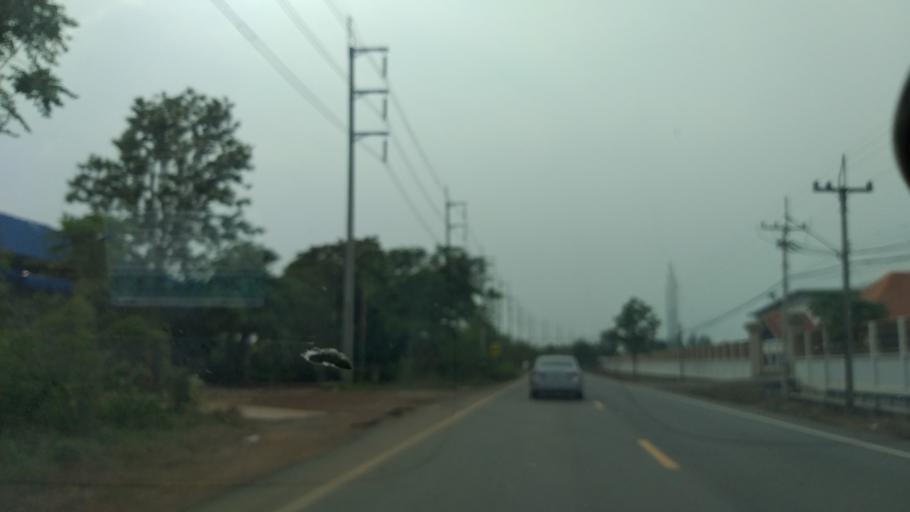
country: TH
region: Chachoengsao
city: Plaeng Yao
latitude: 13.5778
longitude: 101.2400
